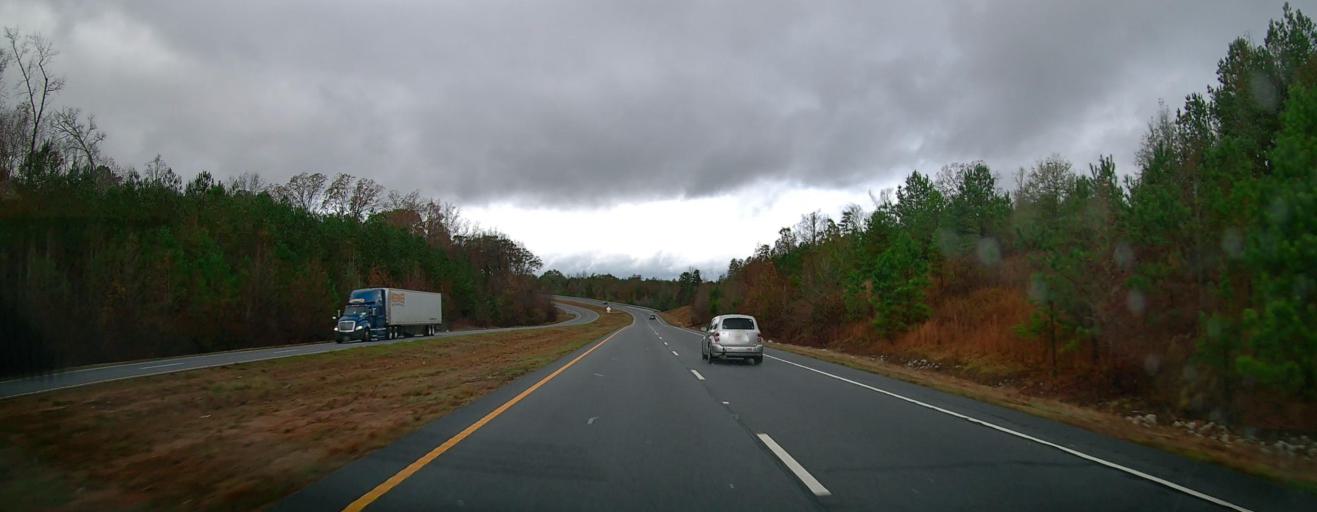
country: US
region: Georgia
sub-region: Jackson County
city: Nicholson
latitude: 34.0557
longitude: -83.4106
